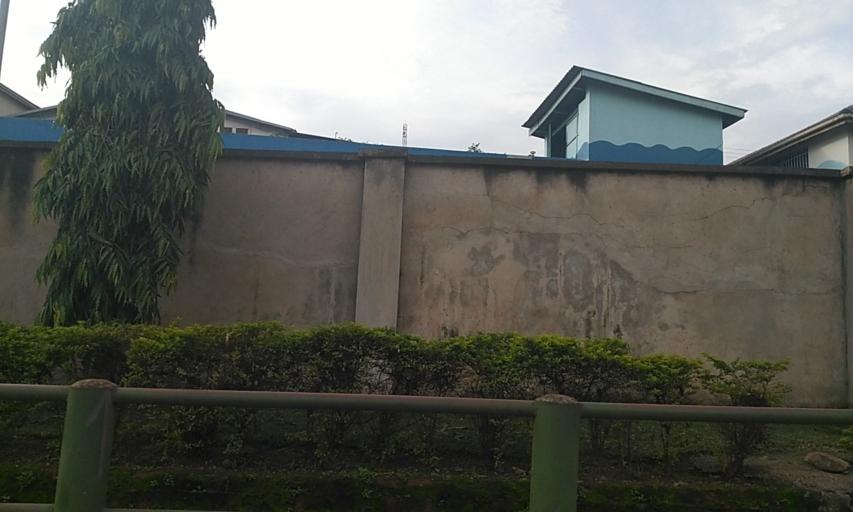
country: UG
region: Central Region
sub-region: Kampala District
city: Kampala
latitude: 0.3145
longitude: 32.5951
